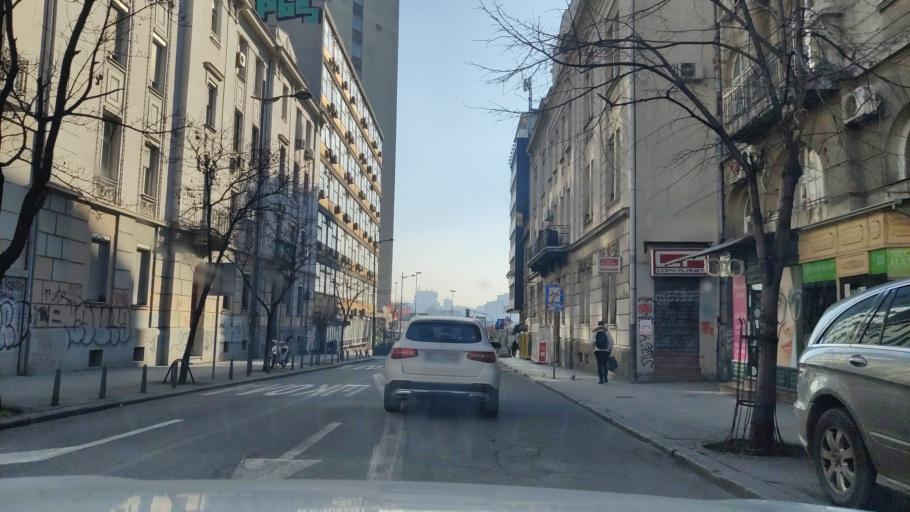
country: RS
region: Central Serbia
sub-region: Belgrade
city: Stari Grad
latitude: 44.8156
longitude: 20.4560
